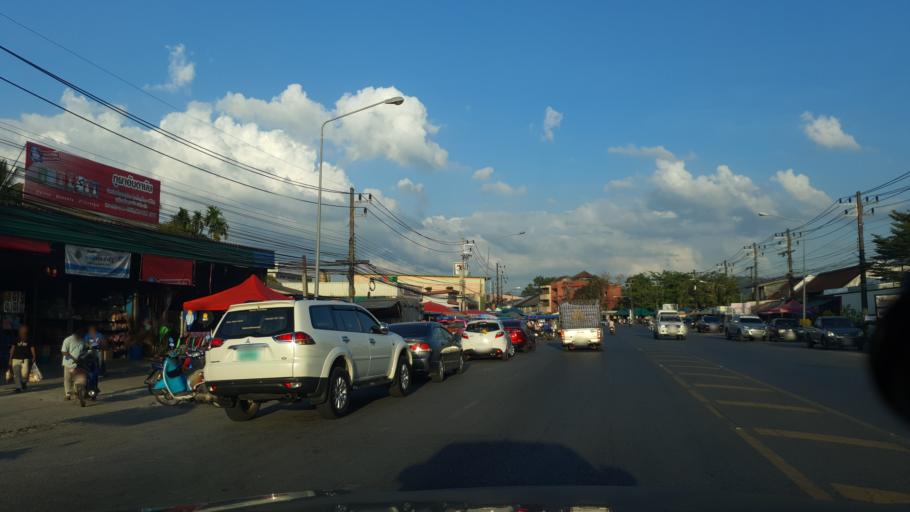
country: TH
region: Phangnga
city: Takua Pa
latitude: 8.8420
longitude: 98.2861
